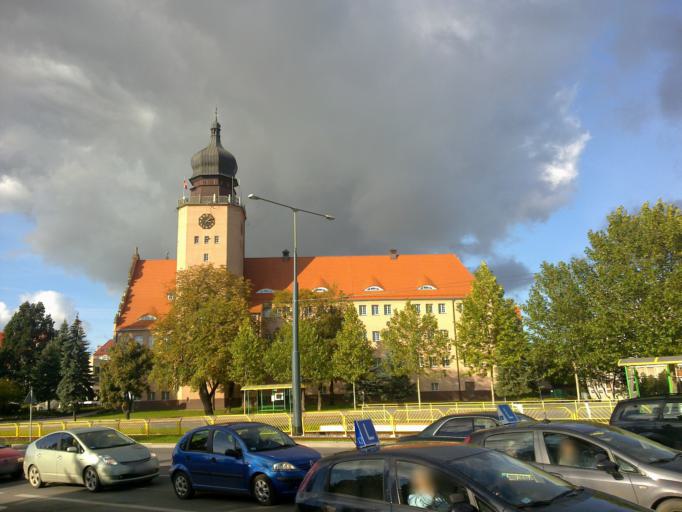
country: PL
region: Warmian-Masurian Voivodeship
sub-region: Powiat elblaski
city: Elblag
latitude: 54.1600
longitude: 19.4085
